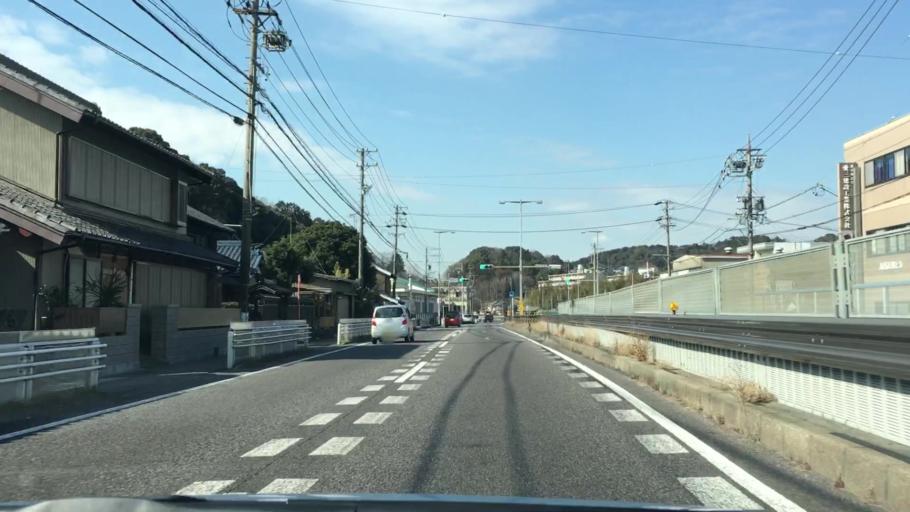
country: JP
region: Aichi
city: Gamagori
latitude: 34.8965
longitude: 137.2507
